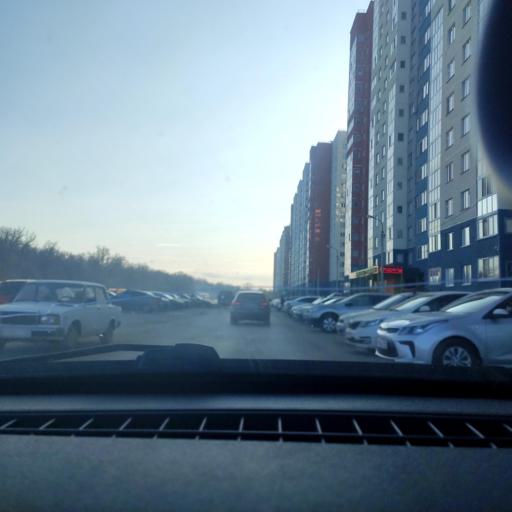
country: RU
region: Bashkortostan
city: Ufa
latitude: 54.7861
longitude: 56.1383
